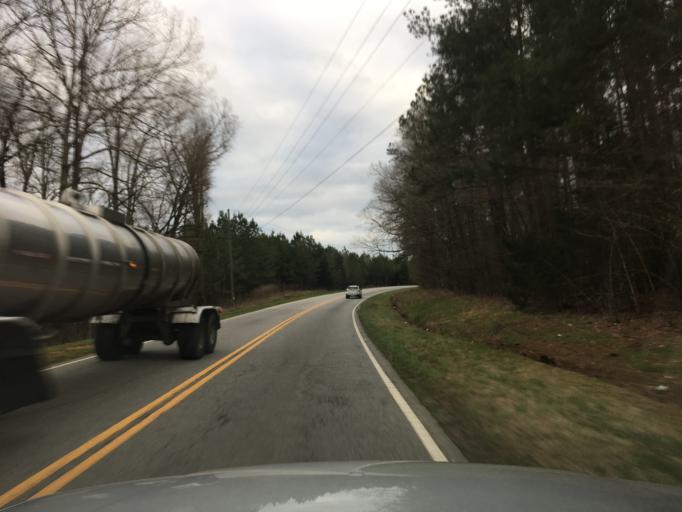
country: US
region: South Carolina
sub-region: Saluda County
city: Saluda
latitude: 33.9850
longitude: -81.7696
